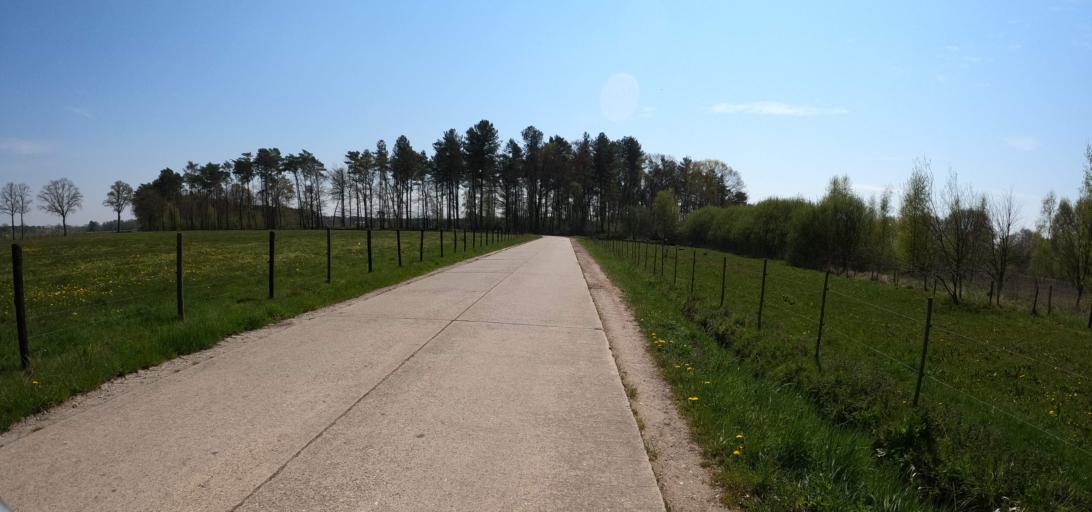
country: BE
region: Flanders
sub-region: Provincie Antwerpen
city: Zoersel
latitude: 51.2424
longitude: 4.7480
